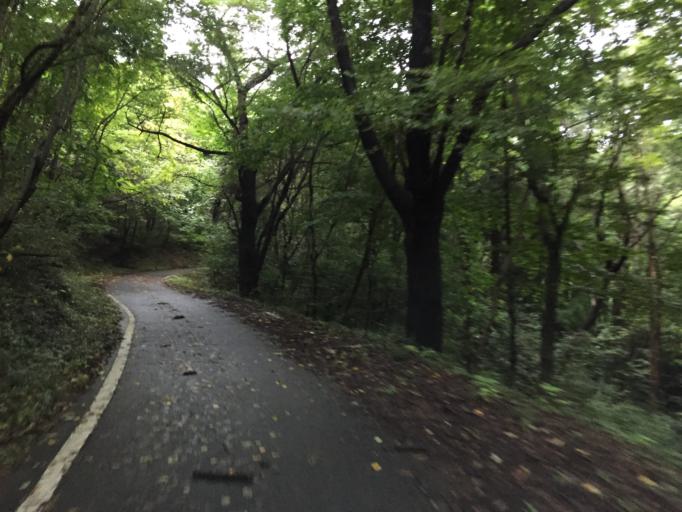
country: JP
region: Fukushima
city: Hobaramachi
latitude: 37.7678
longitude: 140.5241
